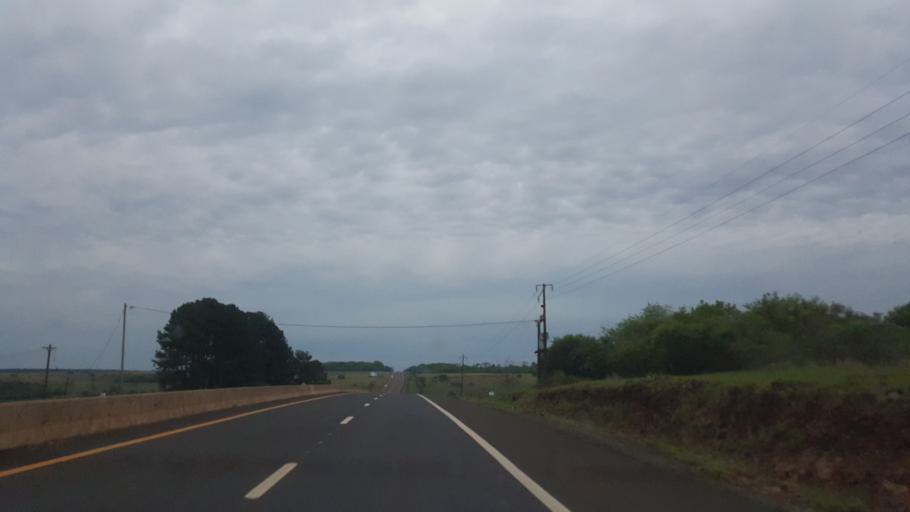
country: AR
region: Misiones
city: Garupa
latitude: -27.5579
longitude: -55.8494
